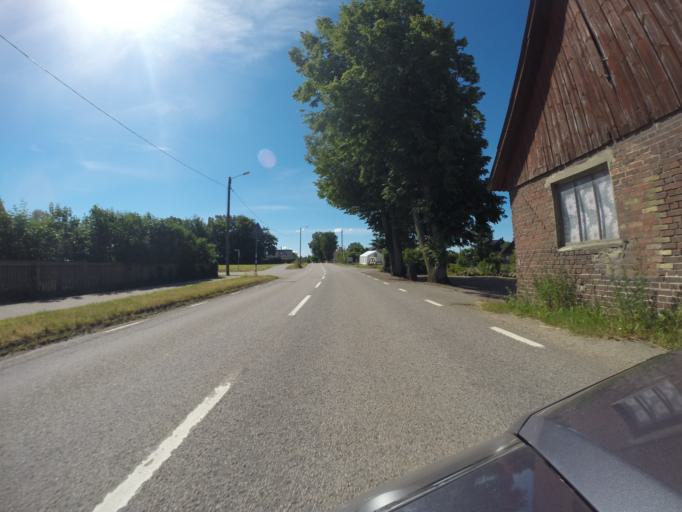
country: SE
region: Skane
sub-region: Helsingborg
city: Odakra
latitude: 56.1213
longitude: 12.6926
